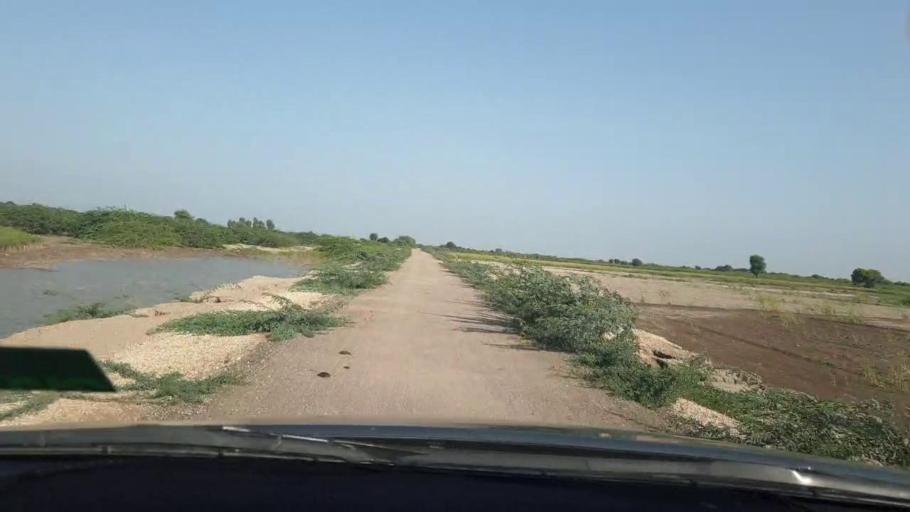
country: PK
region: Sindh
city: Naukot
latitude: 24.8641
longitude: 69.3152
